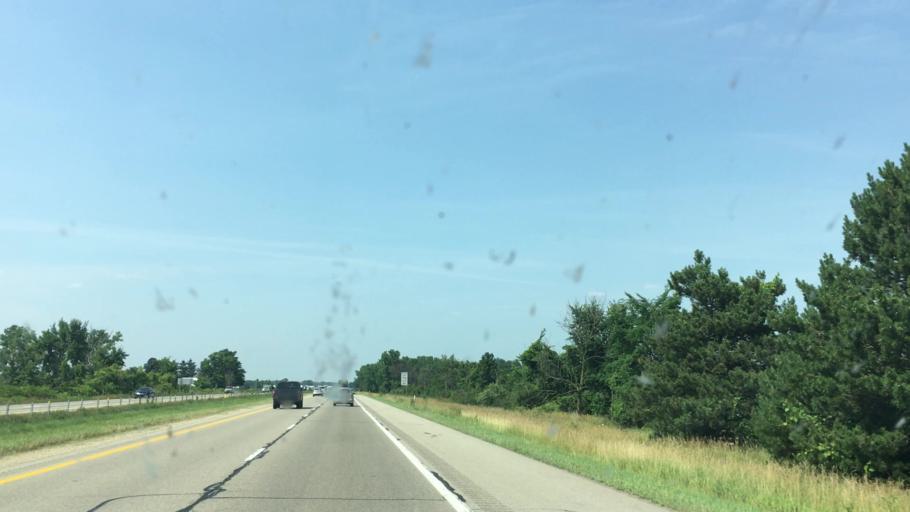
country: US
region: Michigan
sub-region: Allegan County
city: Wayland
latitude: 42.6384
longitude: -85.6621
